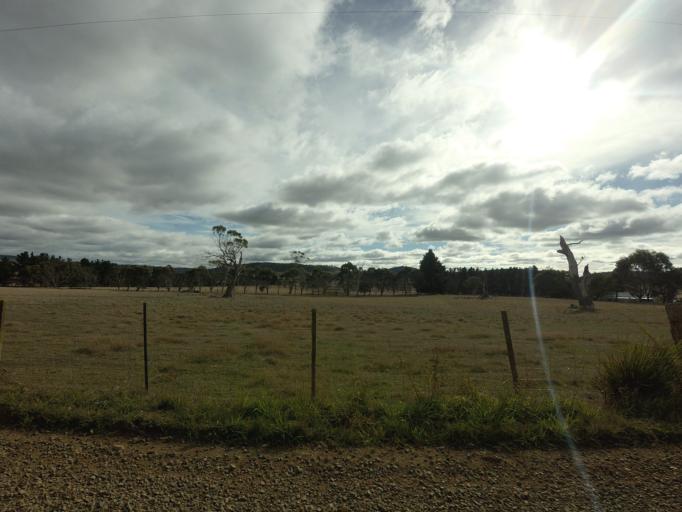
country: AU
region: Tasmania
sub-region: Brighton
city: Bridgewater
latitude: -42.4126
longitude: 147.3985
